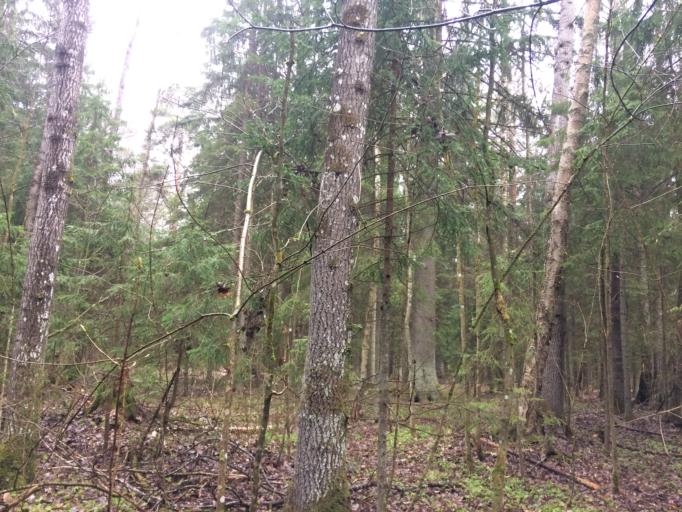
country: RU
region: St.-Petersburg
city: Petrodvorets
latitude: 59.8900
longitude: 29.8365
